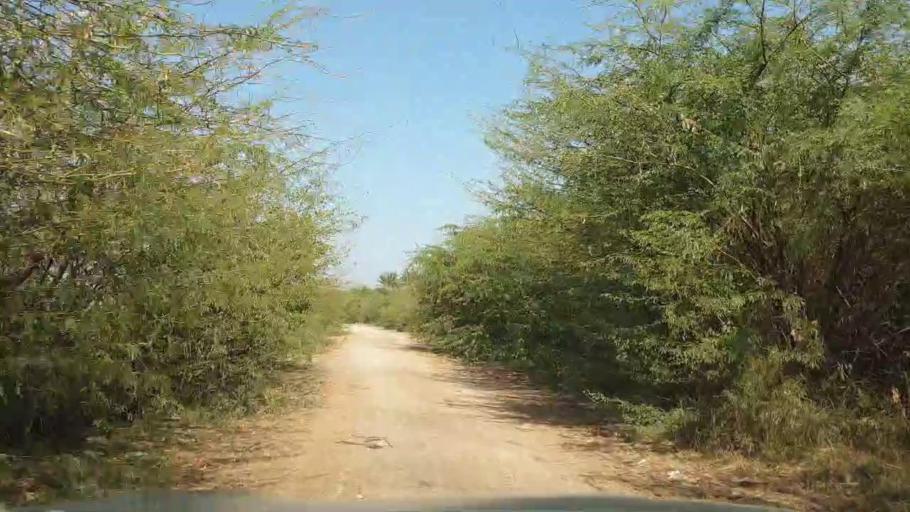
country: PK
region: Sindh
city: Berani
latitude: 25.6799
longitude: 68.8963
